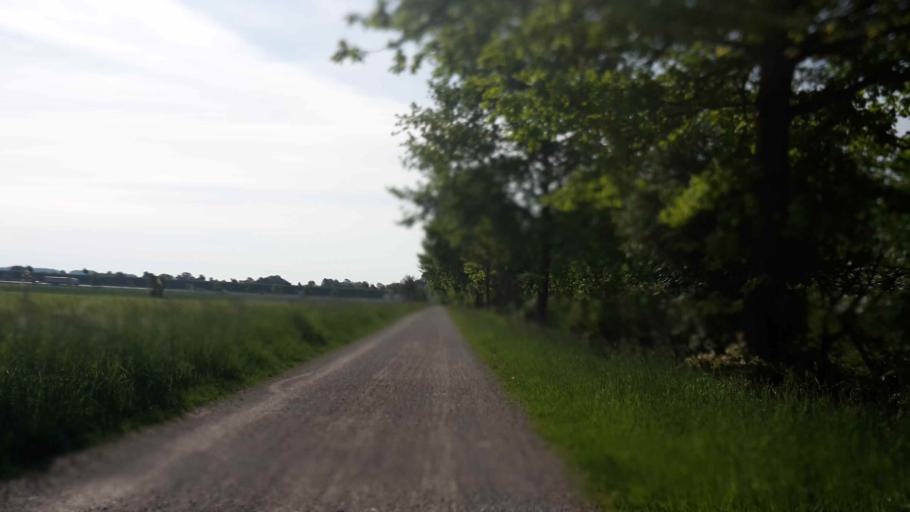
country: DE
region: Bavaria
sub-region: Upper Bavaria
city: Garching bei Munchen
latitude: 48.2402
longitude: 11.6313
